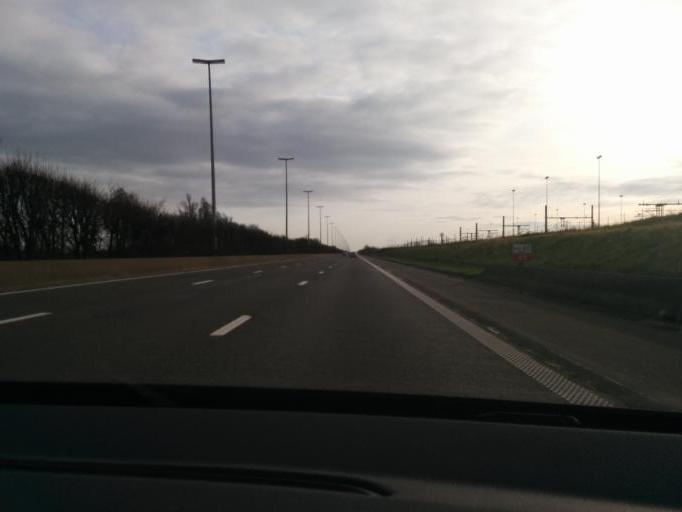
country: BE
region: Flanders
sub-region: Provincie Vlaams-Brabant
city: Tienen
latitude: 50.7686
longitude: 4.9360
